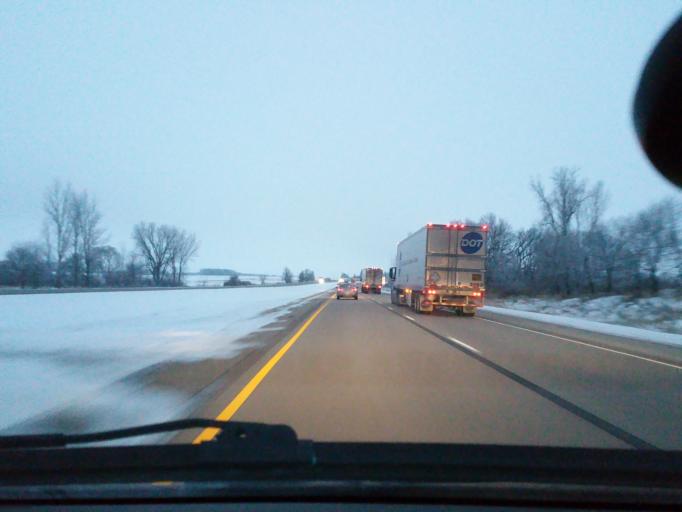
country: US
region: Iowa
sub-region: Worth County
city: Northwood
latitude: 43.4959
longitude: -93.3528
